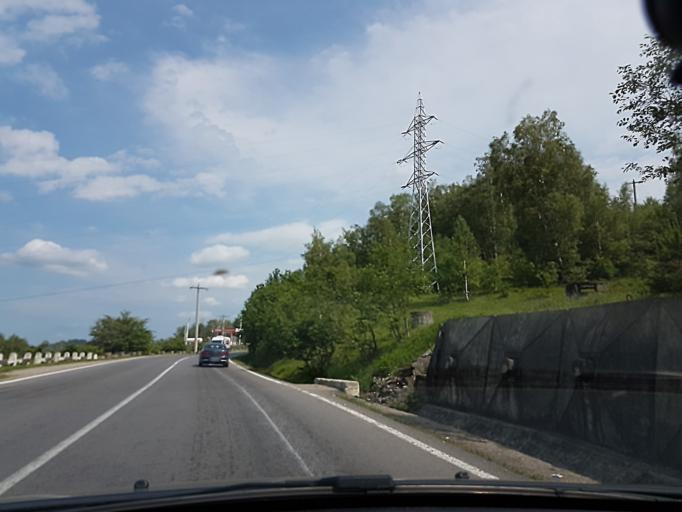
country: RO
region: Prahova
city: Maneciu
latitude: 45.3332
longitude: 25.9667
